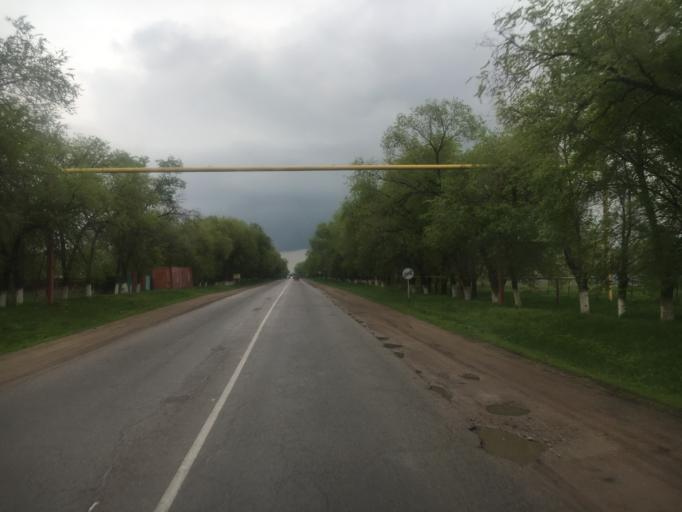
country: KZ
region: Almaty Oblysy
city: Burunday
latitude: 43.2269
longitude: 76.6615
